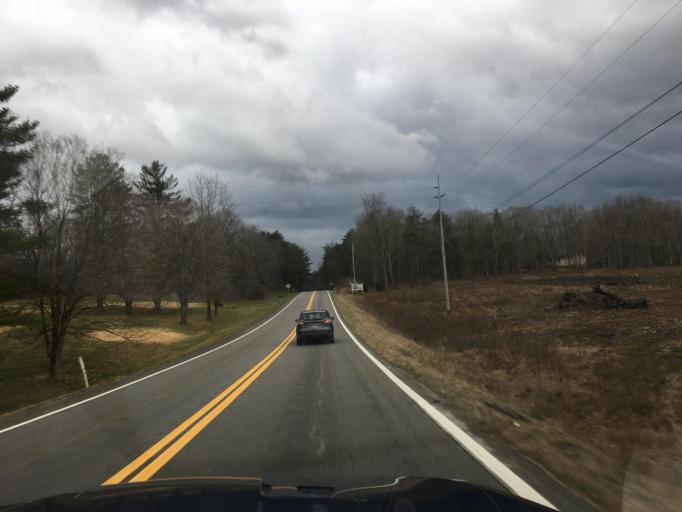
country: US
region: Tennessee
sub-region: Cumberland County
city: Crossville
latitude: 35.8816
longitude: -84.9361
